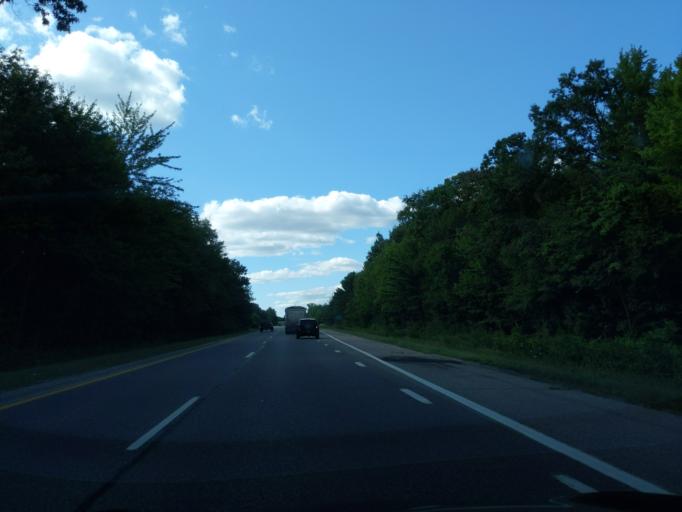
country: US
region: Michigan
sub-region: Muskegon County
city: Fruitport
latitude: 43.1165
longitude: -86.1274
